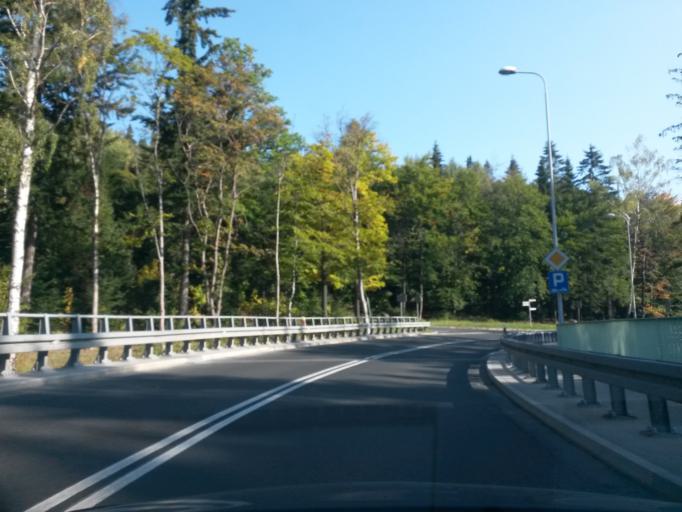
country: PL
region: Lower Silesian Voivodeship
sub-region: Powiat jeleniogorski
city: Szklarska Poreba
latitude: 50.8267
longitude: 15.5079
